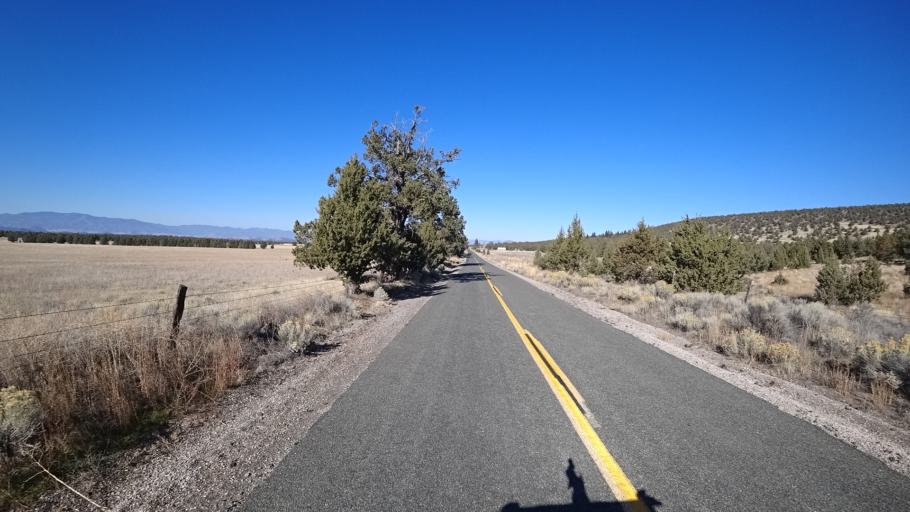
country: US
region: California
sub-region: Siskiyou County
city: Weed
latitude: 41.6144
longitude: -122.3168
